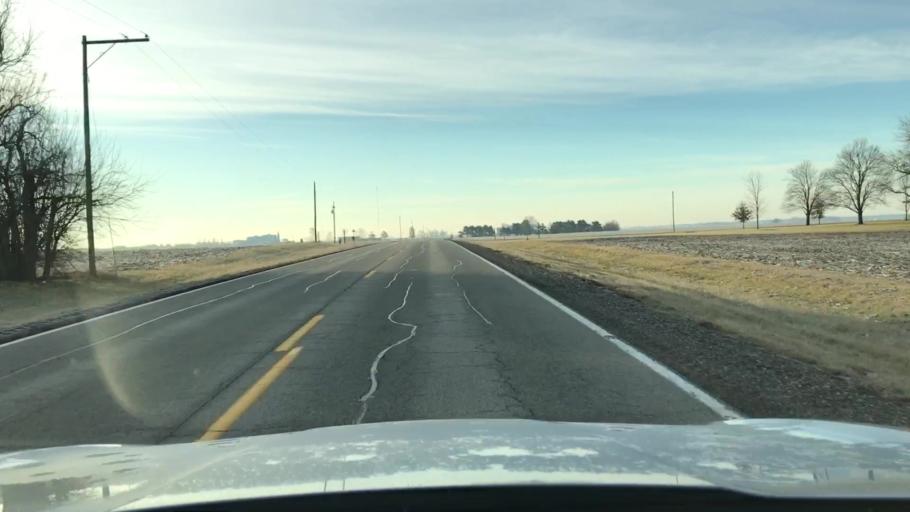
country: US
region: Illinois
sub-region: McLean County
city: Hudson
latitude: 40.5925
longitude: -88.9448
